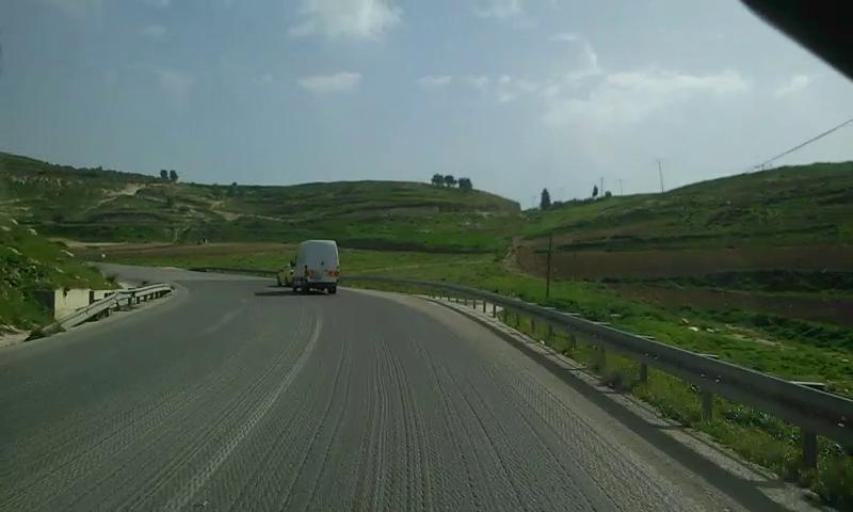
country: PS
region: West Bank
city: `Arrabah
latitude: 32.3848
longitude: 35.2141
